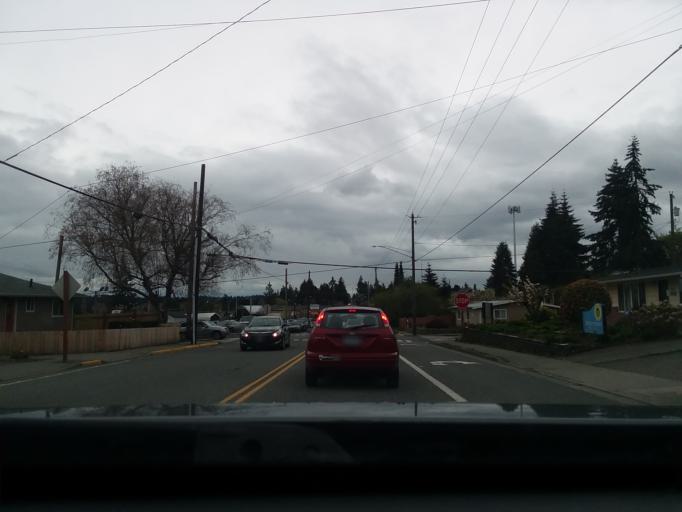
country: US
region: Washington
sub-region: Snohomish County
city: Esperance
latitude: 47.7964
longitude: -122.3356
